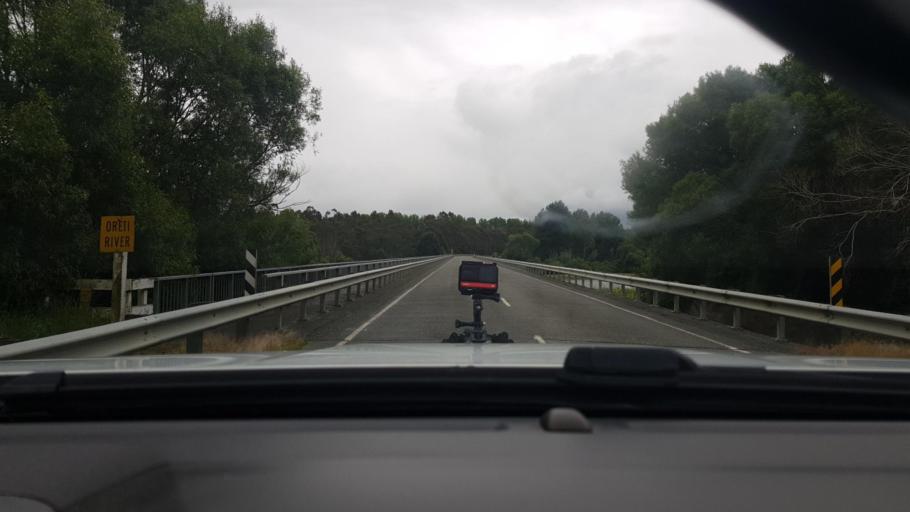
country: NZ
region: Southland
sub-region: Southland District
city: Winton
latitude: -45.8964
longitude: 168.3639
